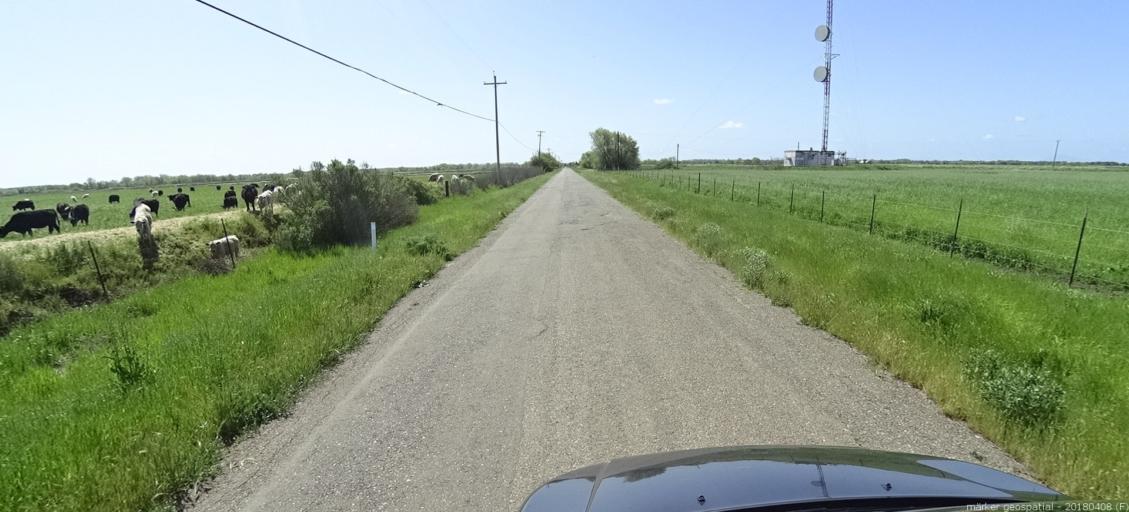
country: US
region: California
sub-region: San Joaquin County
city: Thornton
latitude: 38.2844
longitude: -121.4198
